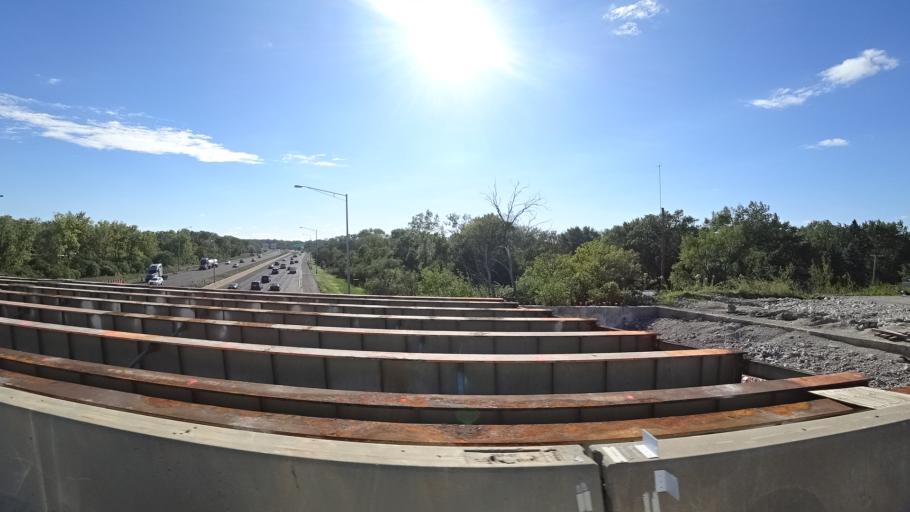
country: US
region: Illinois
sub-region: Cook County
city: Country Club Hills
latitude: 41.5827
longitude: -87.7346
